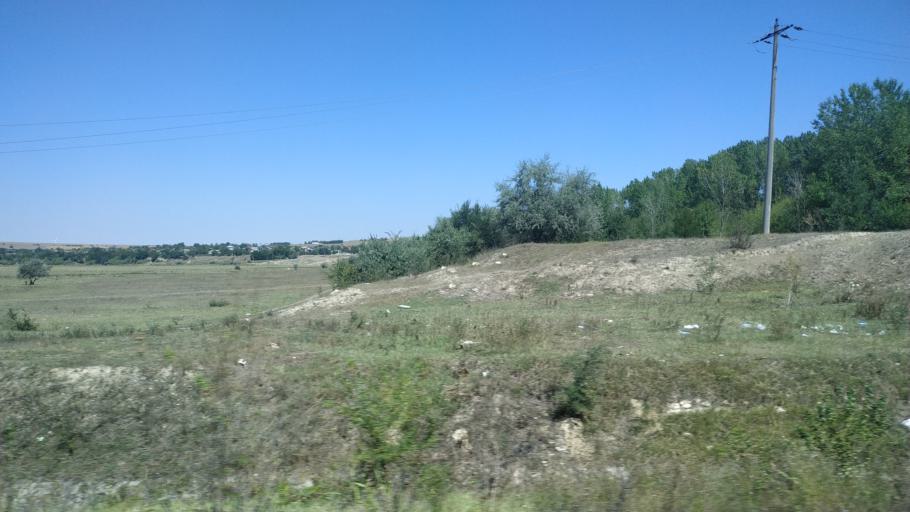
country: RO
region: Constanta
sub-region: Comuna Mircea Voda
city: Satu Nou
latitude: 44.2569
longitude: 28.2328
